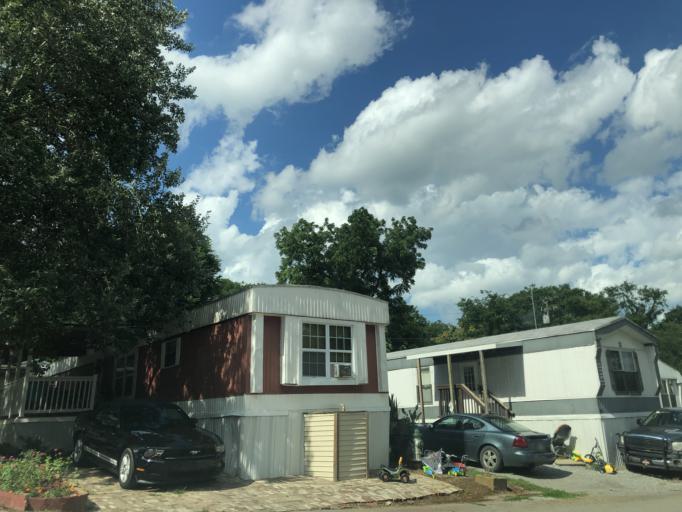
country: US
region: Tennessee
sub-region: Davidson County
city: Nashville
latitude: 36.2087
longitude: -86.7735
